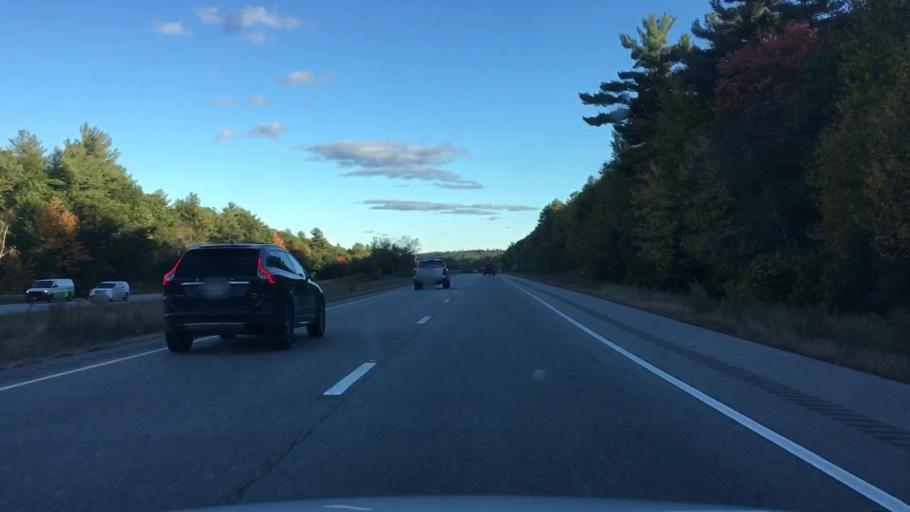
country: US
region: New Hampshire
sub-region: Rockingham County
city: Candia
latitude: 43.0409
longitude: -71.2655
